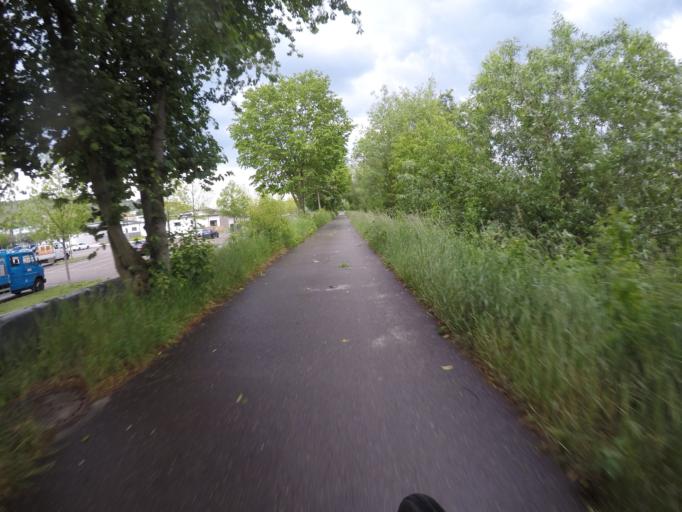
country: DE
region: Baden-Wuerttemberg
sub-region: Regierungsbezirk Stuttgart
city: Ostfildern
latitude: 48.7458
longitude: 9.2708
